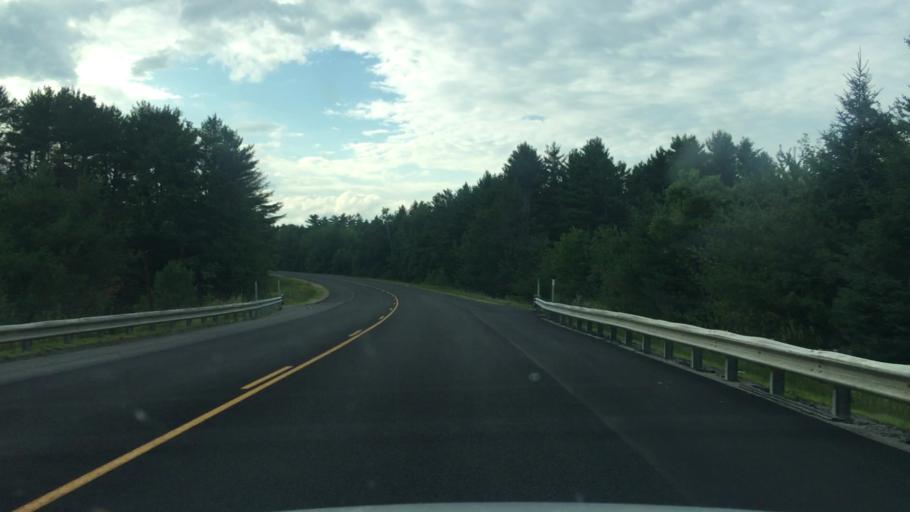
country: US
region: Maine
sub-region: Waldo County
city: Palermo
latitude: 44.4075
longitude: -69.4806
